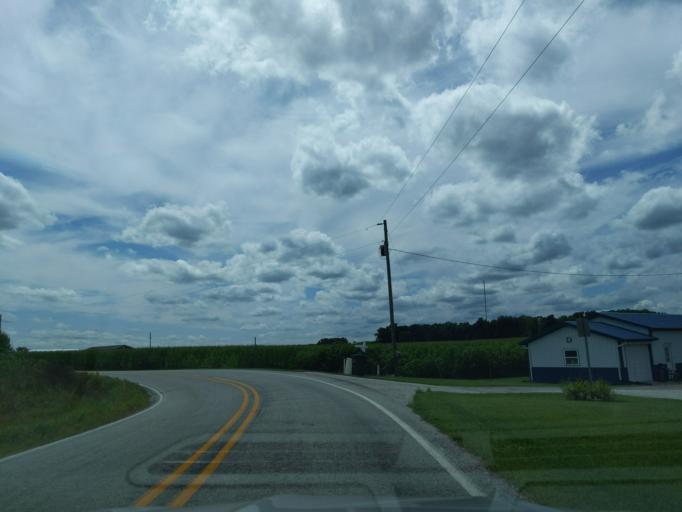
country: US
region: Indiana
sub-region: Ripley County
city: Osgood
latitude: 39.2060
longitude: -85.2774
